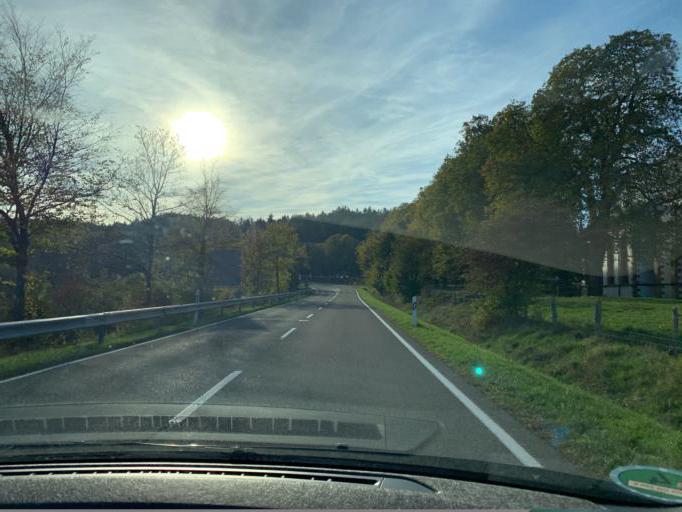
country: DE
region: North Rhine-Westphalia
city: Heimbach
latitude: 50.6190
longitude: 6.4813
